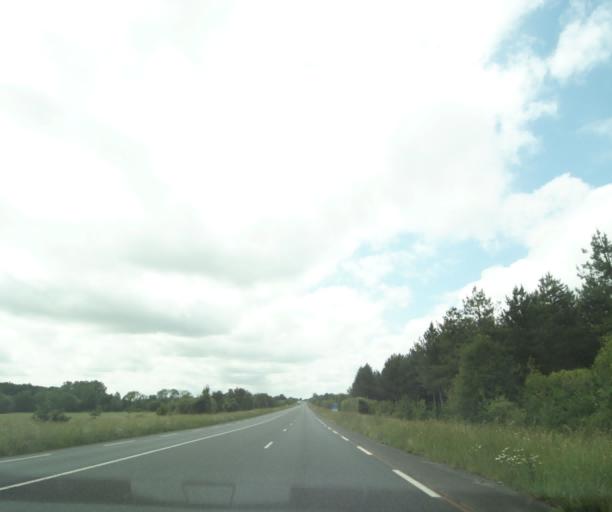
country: FR
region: Poitou-Charentes
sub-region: Departement des Deux-Sevres
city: Airvault
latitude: 46.7899
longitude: -0.2148
